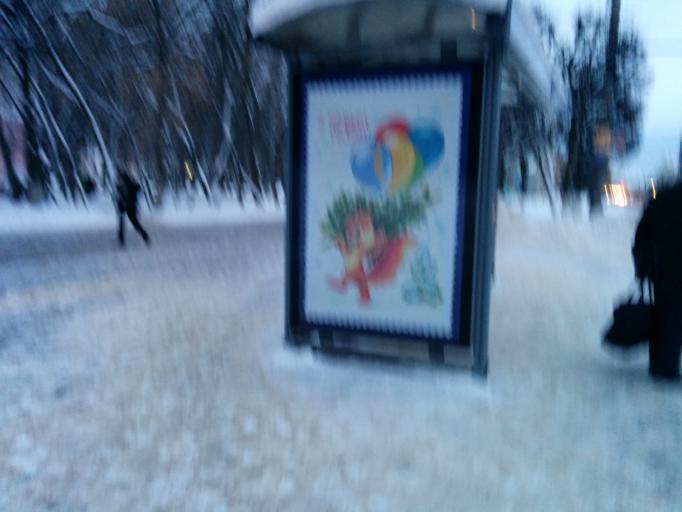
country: RU
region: Chuvashia
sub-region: Cheboksarskiy Rayon
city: Cheboksary
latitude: 56.1288
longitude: 47.2486
